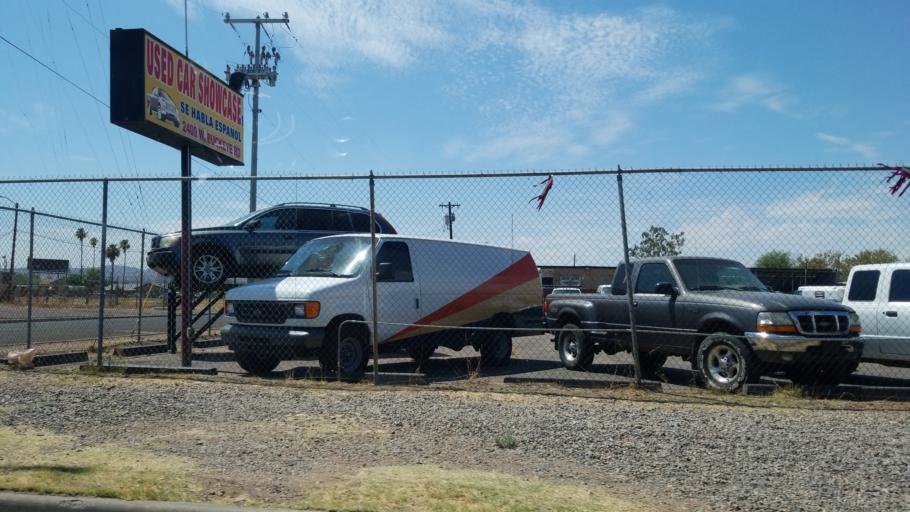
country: US
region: Arizona
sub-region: Maricopa County
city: Phoenix
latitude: 33.4367
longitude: -112.1110
